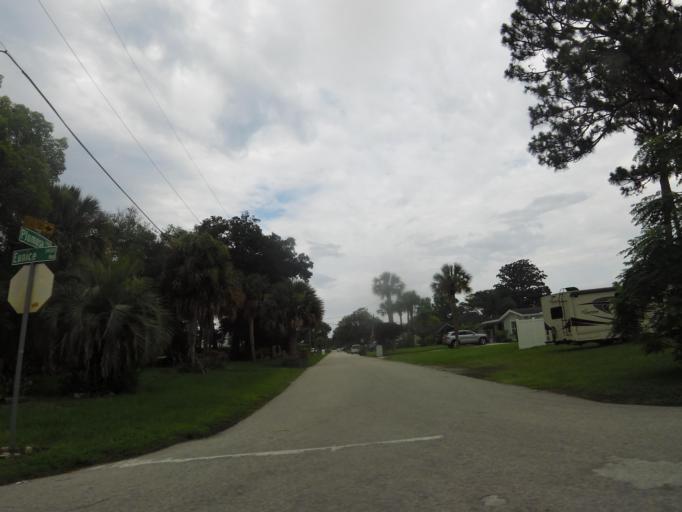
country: US
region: Florida
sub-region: Duval County
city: Jacksonville Beach
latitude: 30.2827
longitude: -81.4338
